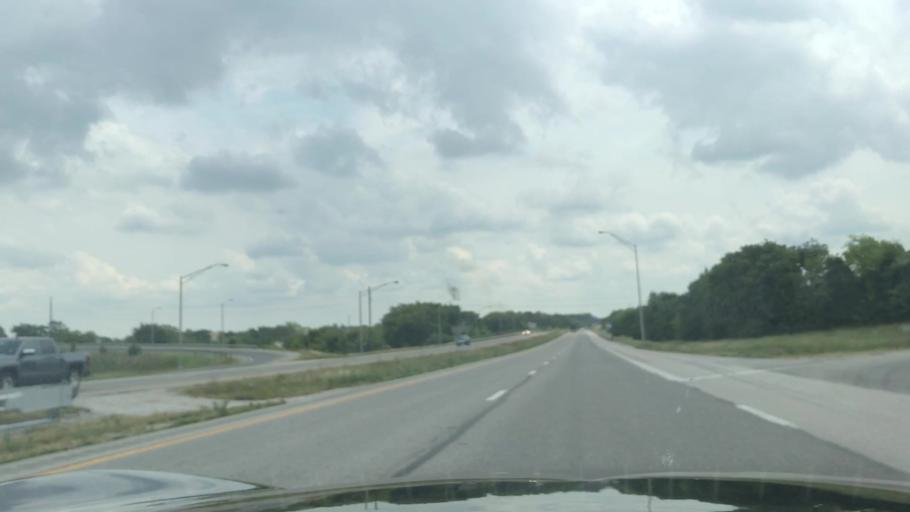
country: US
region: Kentucky
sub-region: Warren County
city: Bowling Green
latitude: 36.9920
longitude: -86.5041
